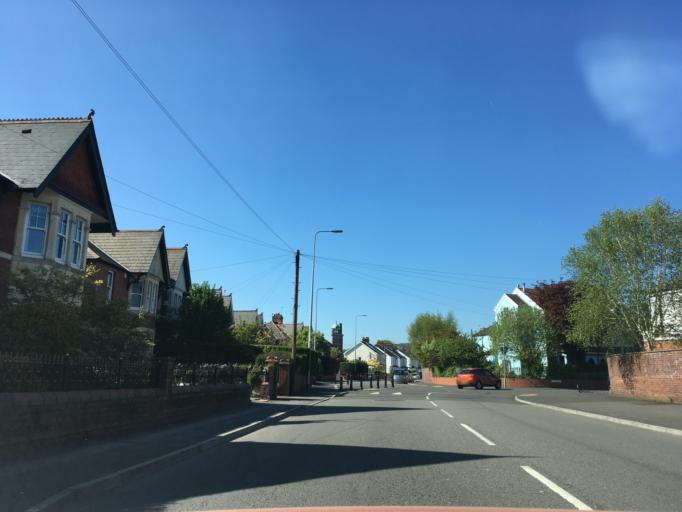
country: GB
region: Wales
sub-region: Cardiff
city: Radyr
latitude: 51.5131
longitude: -3.2286
